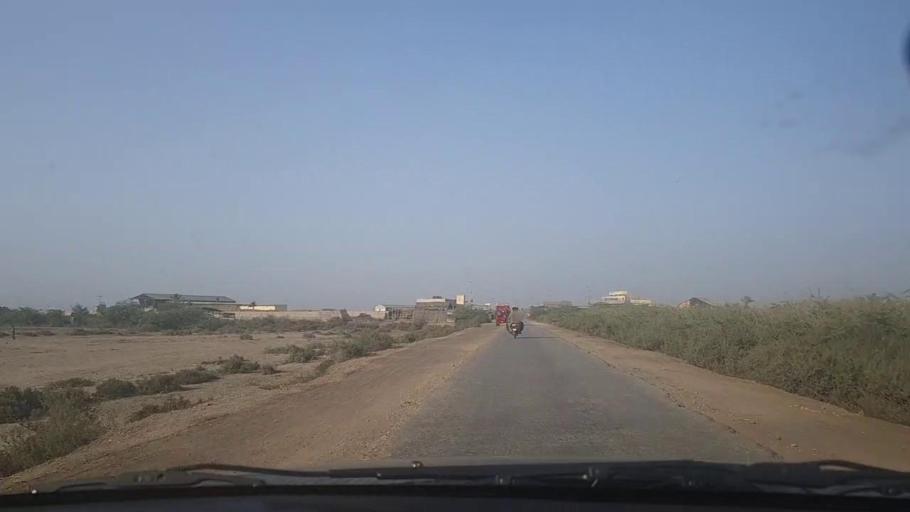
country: PK
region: Sindh
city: Keti Bandar
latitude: 24.3120
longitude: 67.6108
